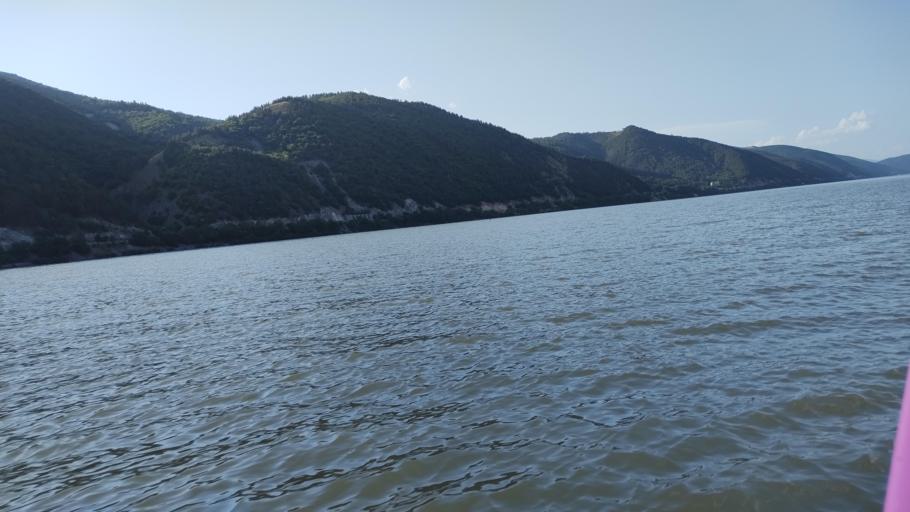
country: RO
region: Mehedinti
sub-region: Comuna Svinita
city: Svinita
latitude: 44.5021
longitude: 22.1929
